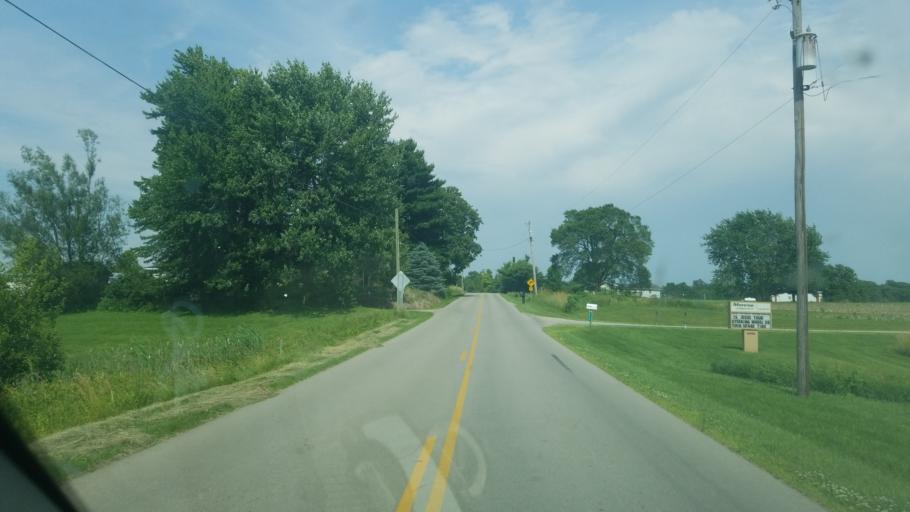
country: US
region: Ohio
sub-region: Logan County
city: West Liberty
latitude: 40.3002
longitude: -83.6589
